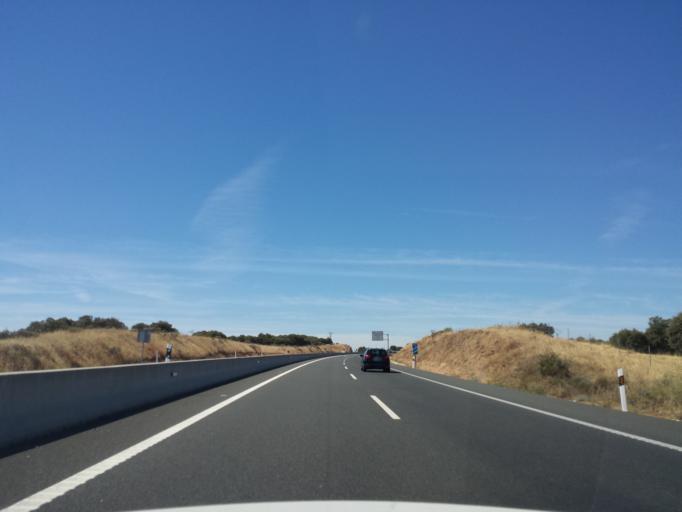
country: ES
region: Extremadura
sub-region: Provincia de Caceres
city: Jaraicejo
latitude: 39.6345
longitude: -5.8146
